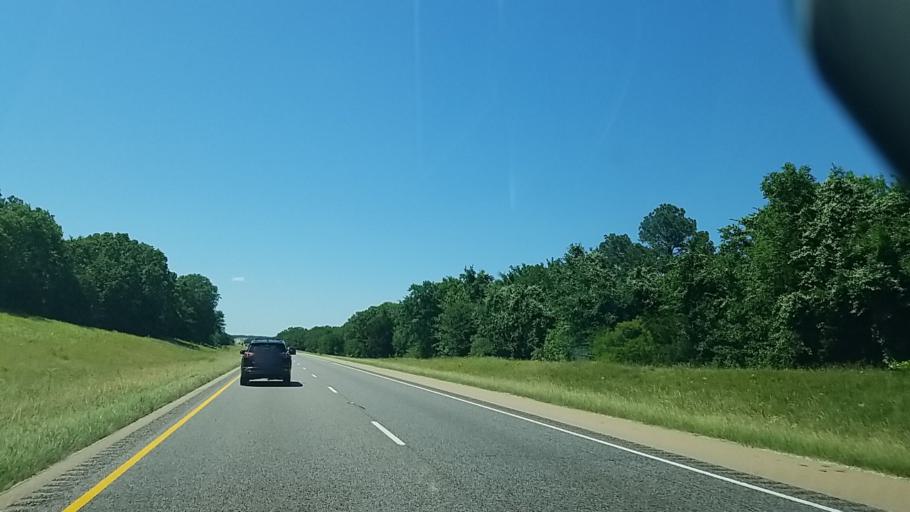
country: US
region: Texas
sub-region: Leon County
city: Buffalo
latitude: 31.5518
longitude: -96.1290
